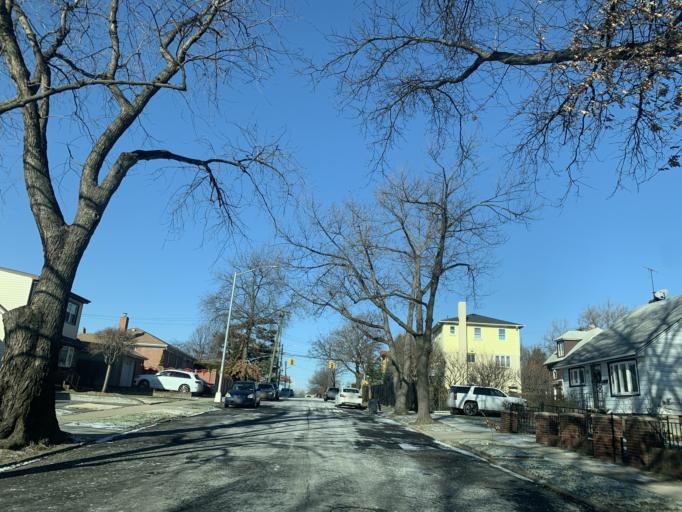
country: US
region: New York
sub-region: Bronx
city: The Bronx
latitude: 40.7859
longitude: -73.8271
